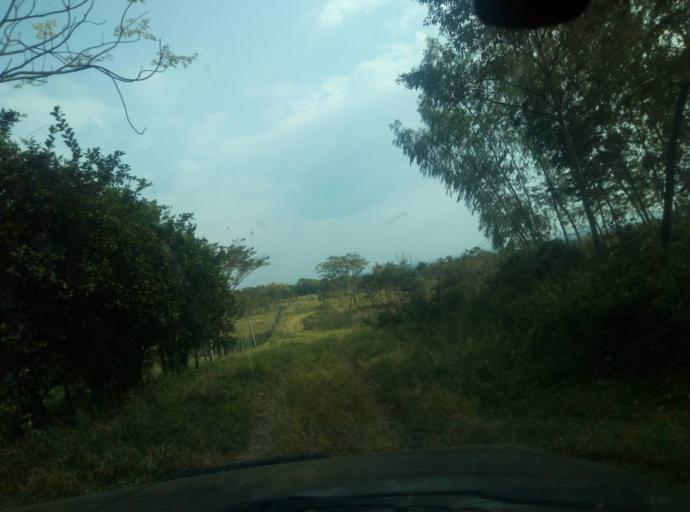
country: PY
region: Caaguazu
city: Doctor Cecilio Baez
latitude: -25.1818
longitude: -56.1346
